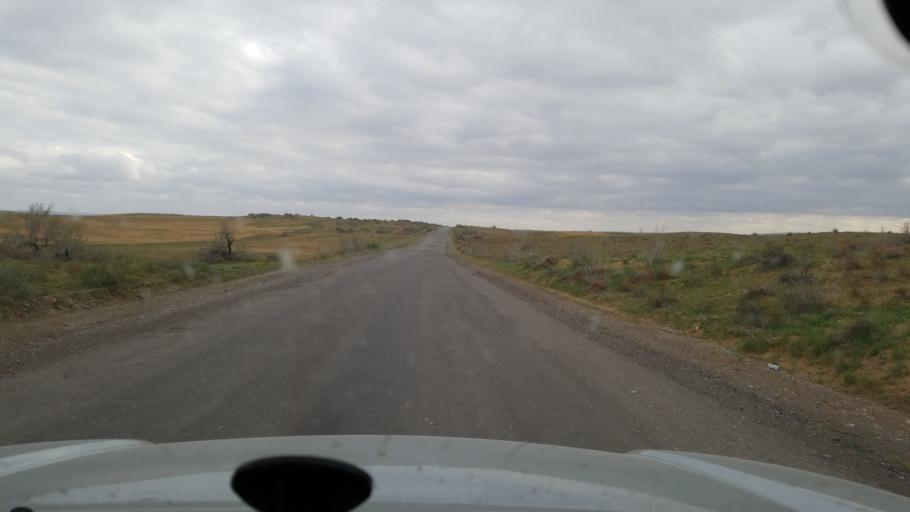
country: TM
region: Mary
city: Serhetabat
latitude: 36.0463
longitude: 62.6168
